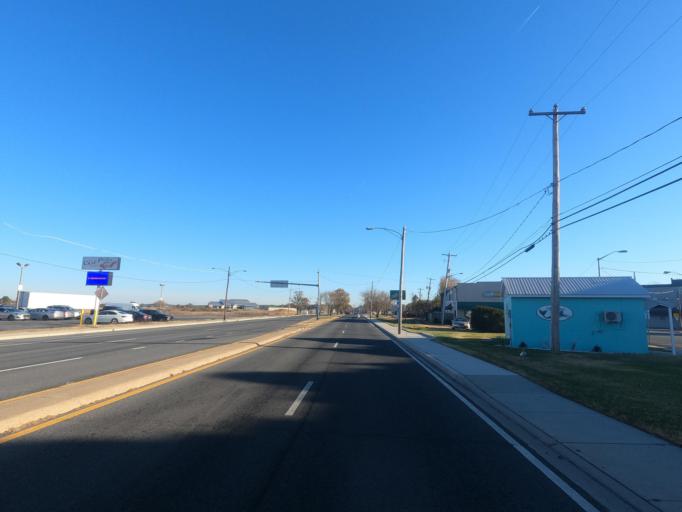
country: US
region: Maryland
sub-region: Somerset County
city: Crisfield
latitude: 37.9817
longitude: -75.8564
